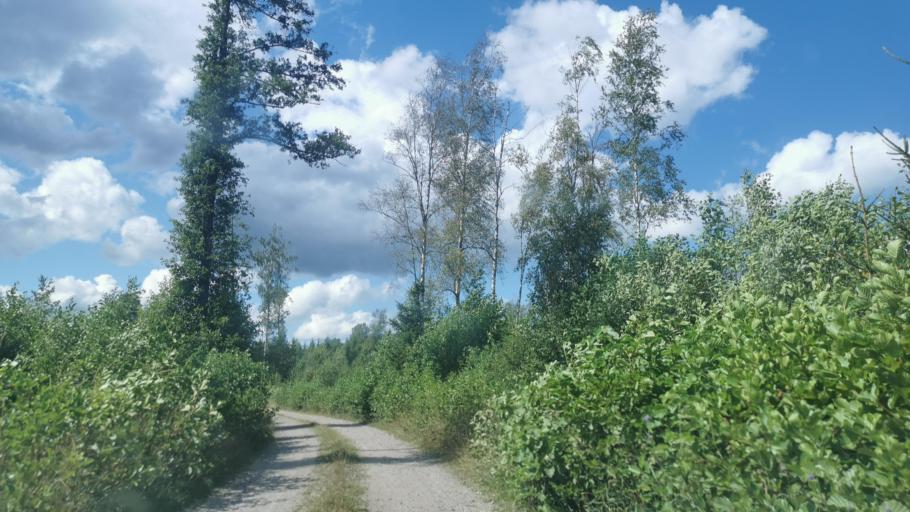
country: SE
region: OEstergoetland
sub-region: Finspangs Kommun
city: Finspang
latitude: 58.7985
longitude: 15.7895
